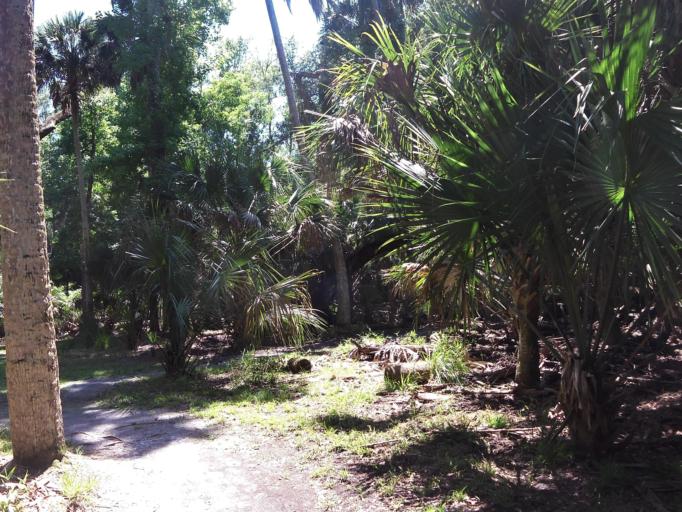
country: US
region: Florida
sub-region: Flagler County
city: Flagler Beach
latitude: 29.4358
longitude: -81.1442
